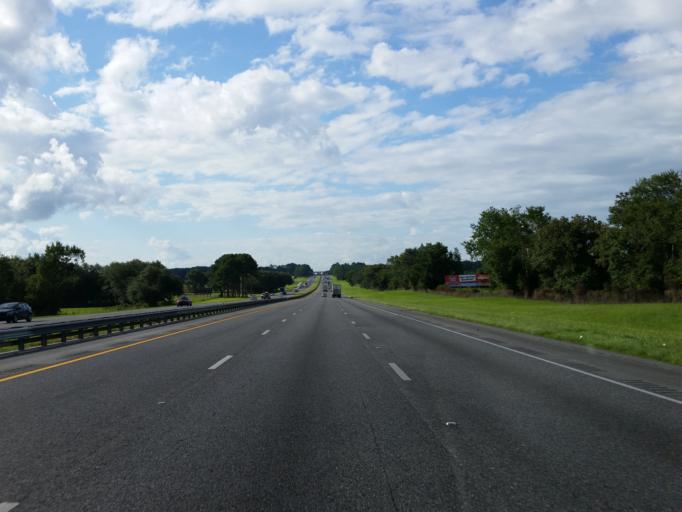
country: US
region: Florida
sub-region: Columbia County
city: Lake City
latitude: 30.0556
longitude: -82.6235
